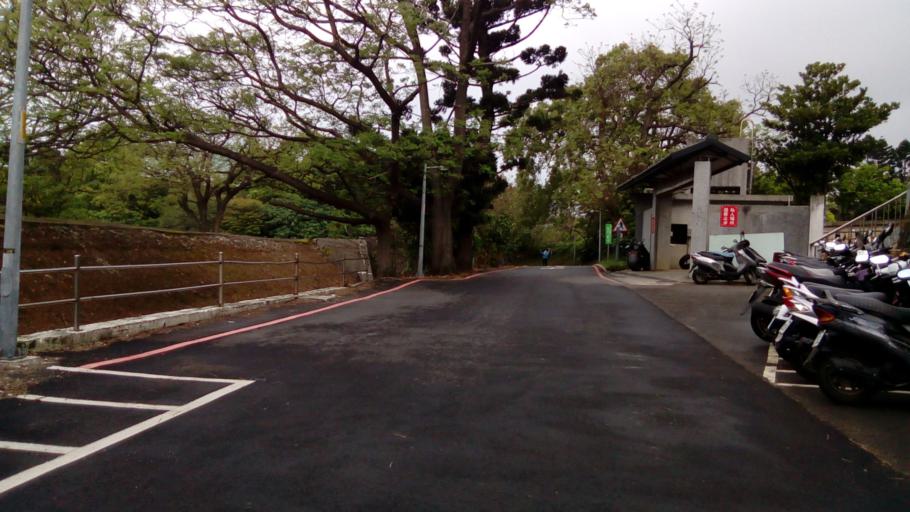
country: TW
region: Taipei
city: Taipei
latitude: 25.1793
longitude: 121.4301
